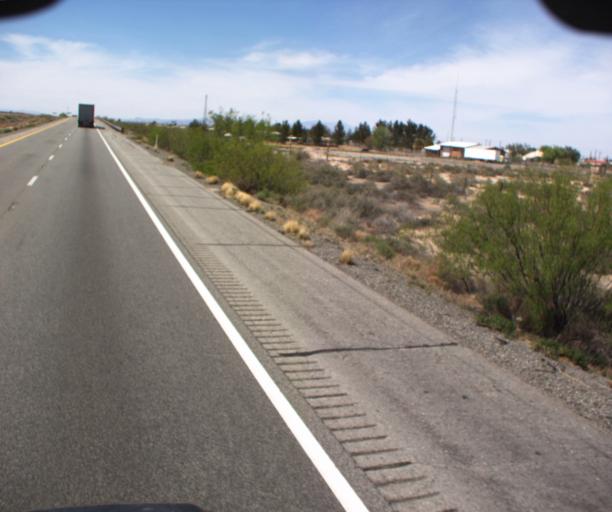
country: US
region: New Mexico
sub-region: Hidalgo County
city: Lordsburg
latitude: 32.2623
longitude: -109.2229
